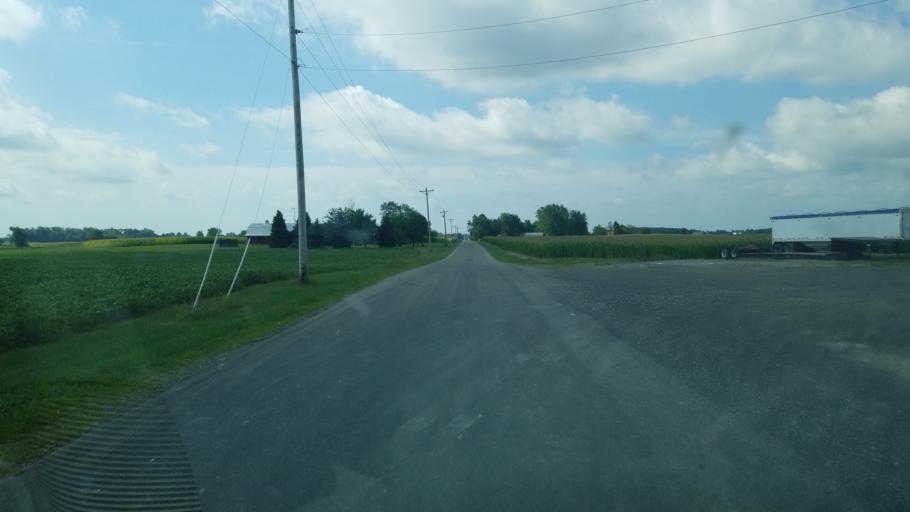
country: US
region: Ohio
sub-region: Hardin County
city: Kenton
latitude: 40.5991
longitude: -83.4453
